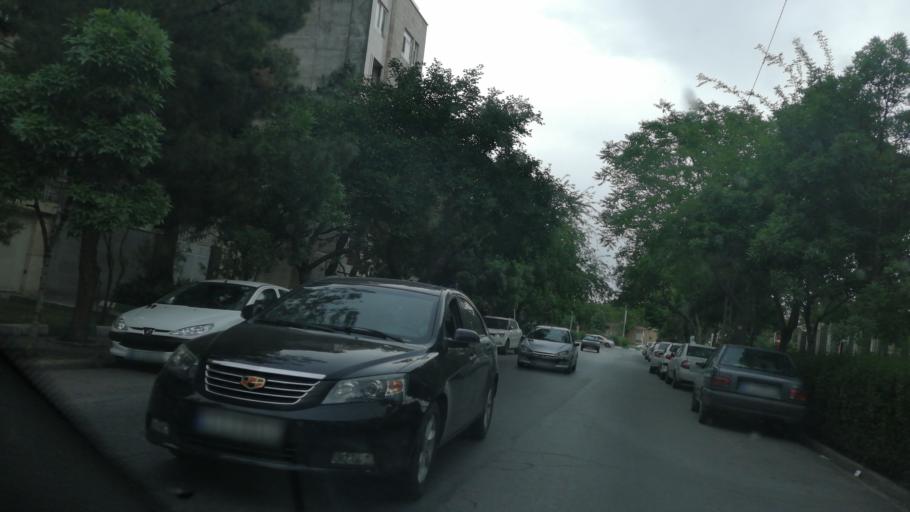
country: IR
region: Razavi Khorasan
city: Mashhad
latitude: 36.2871
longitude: 59.5819
